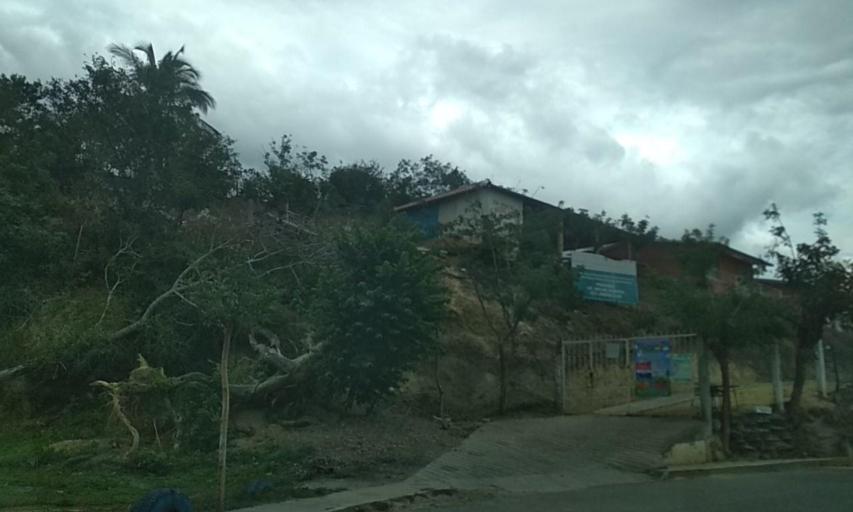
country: MX
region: Veracruz
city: Papantla de Olarte
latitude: 20.4581
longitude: -97.3177
